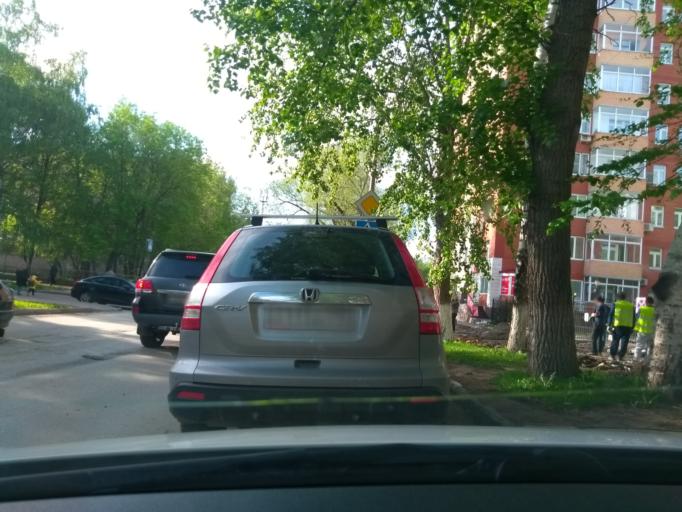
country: RU
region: Perm
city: Perm
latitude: 58.0010
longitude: 56.2542
